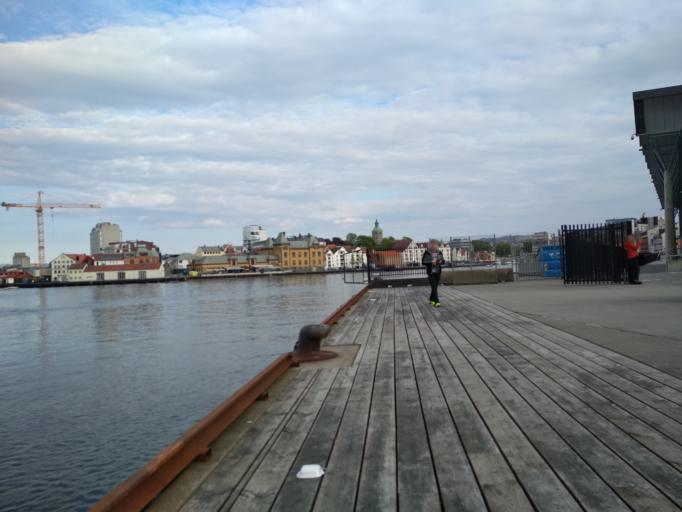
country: NO
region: Rogaland
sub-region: Stavanger
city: Stavanger
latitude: 58.9752
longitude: 5.7248
